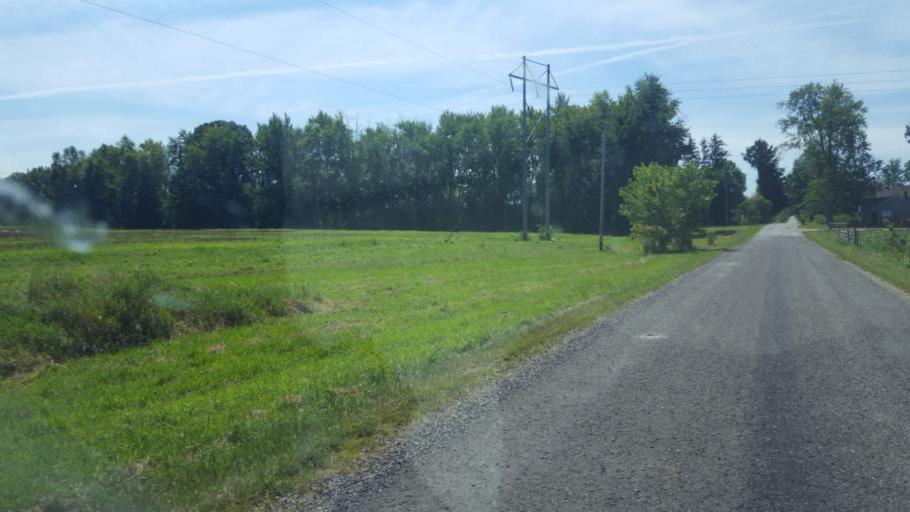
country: US
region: Ohio
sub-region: Knox County
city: Centerburg
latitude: 40.4326
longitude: -82.7377
